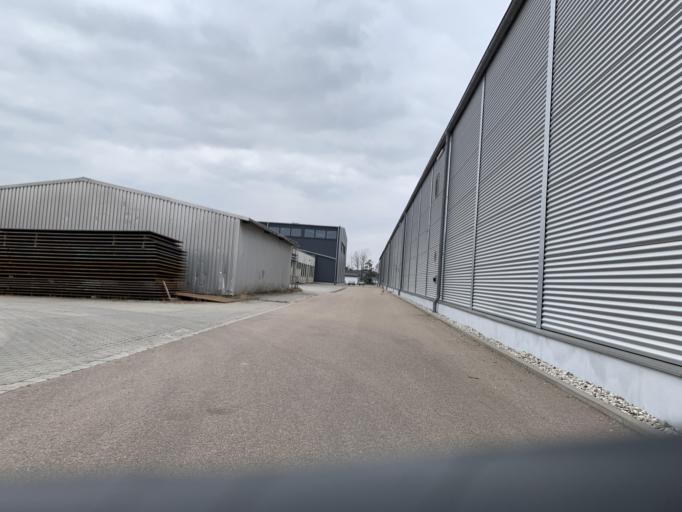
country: DE
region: Bavaria
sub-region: Upper Palatinate
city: Neunburg vorm Wald
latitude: 49.3370
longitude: 12.3979
